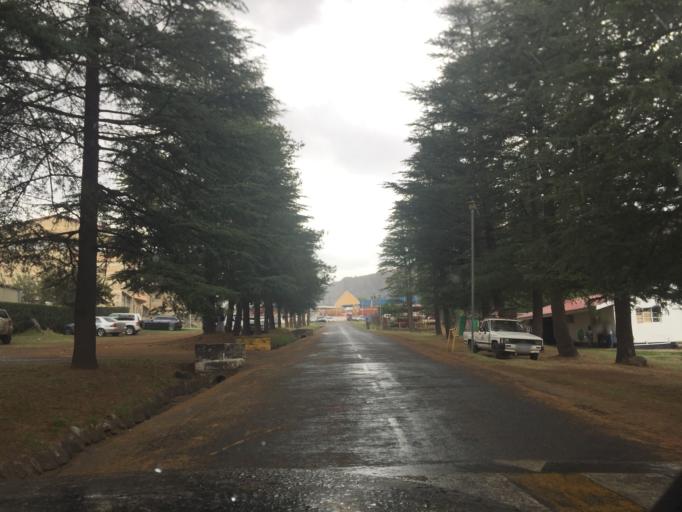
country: LS
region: Maseru
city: Nako
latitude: -29.4495
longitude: 27.7204
